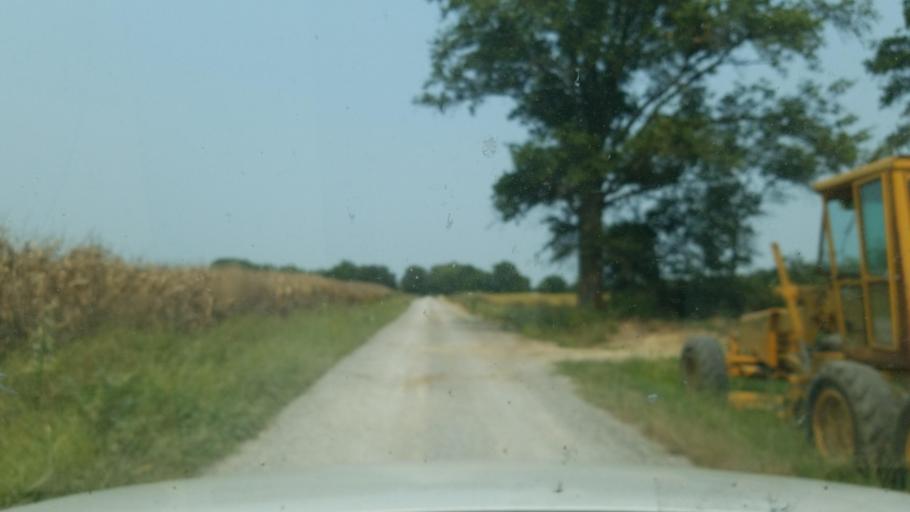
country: US
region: Illinois
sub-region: Saline County
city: Eldorado
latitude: 37.8194
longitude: -88.5167
